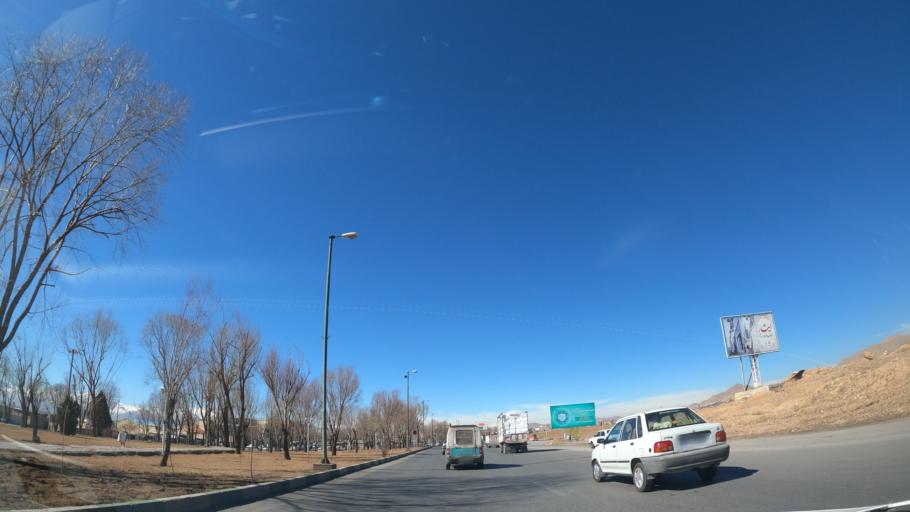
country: IR
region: Chahar Mahall va Bakhtiari
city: Shahrekord
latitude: 32.3074
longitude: 50.9046
